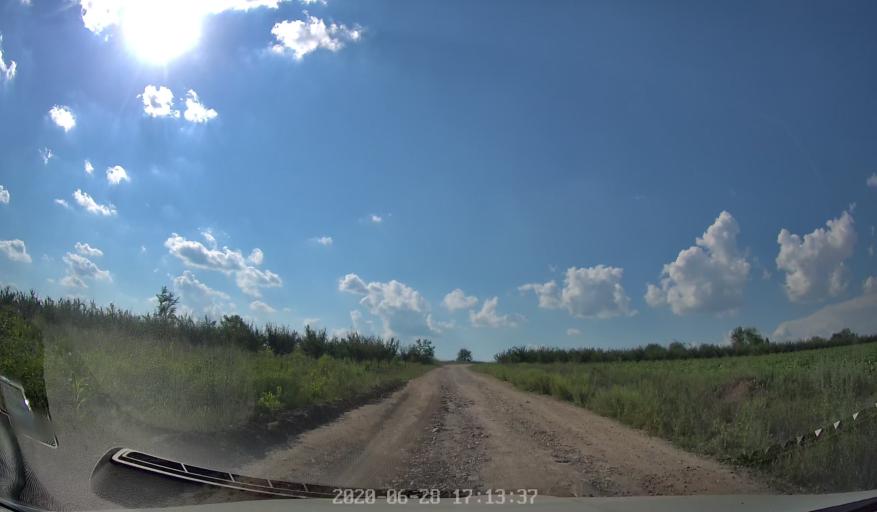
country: MD
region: Chisinau
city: Vatra
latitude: 46.9911
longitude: 28.6967
